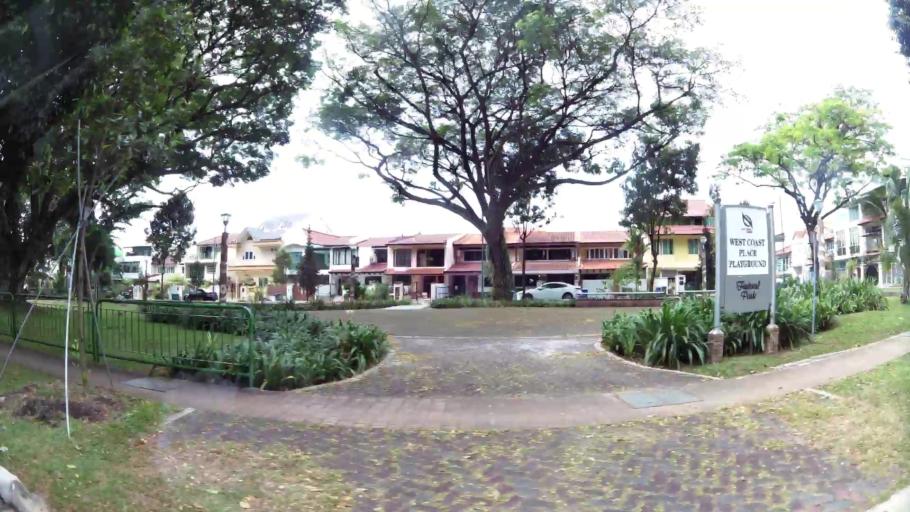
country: SG
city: Singapore
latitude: 1.3150
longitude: 103.7580
